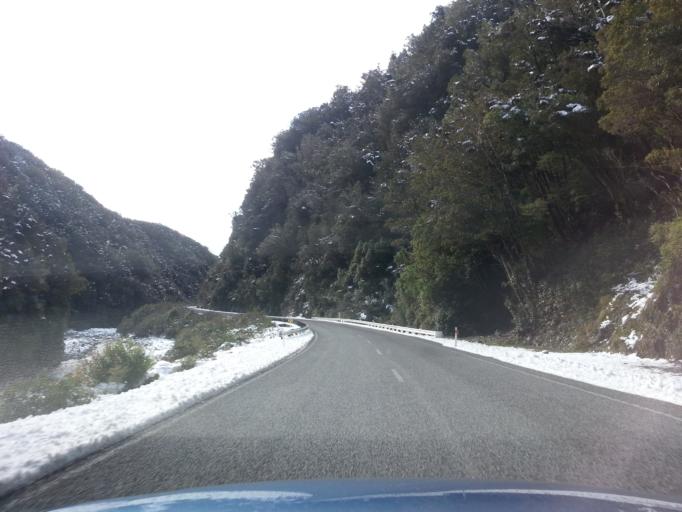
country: NZ
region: West Coast
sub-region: Grey District
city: Greymouth
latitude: -42.8638
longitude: 171.5579
